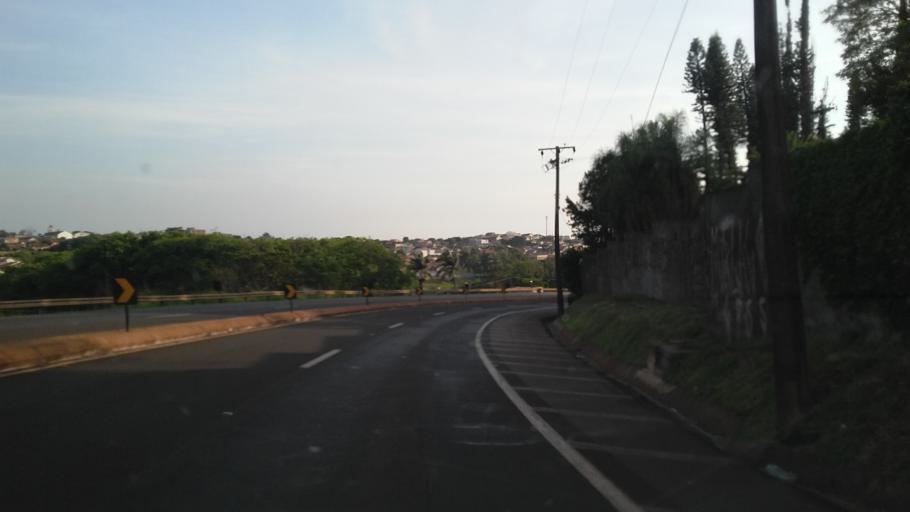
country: BR
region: Parana
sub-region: Assai
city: Assai
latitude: -23.1835
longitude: -50.6392
